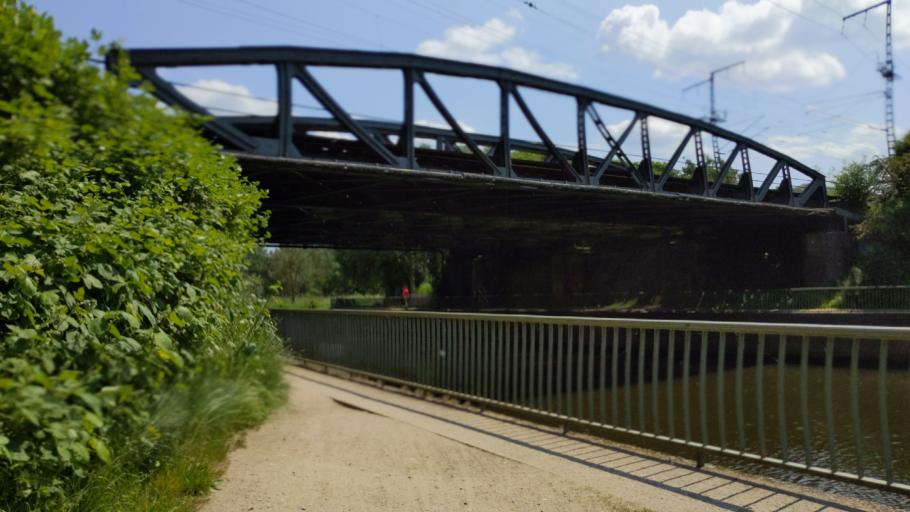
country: DE
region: Schleswig-Holstein
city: Luebeck
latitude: 53.8456
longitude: 10.6559
